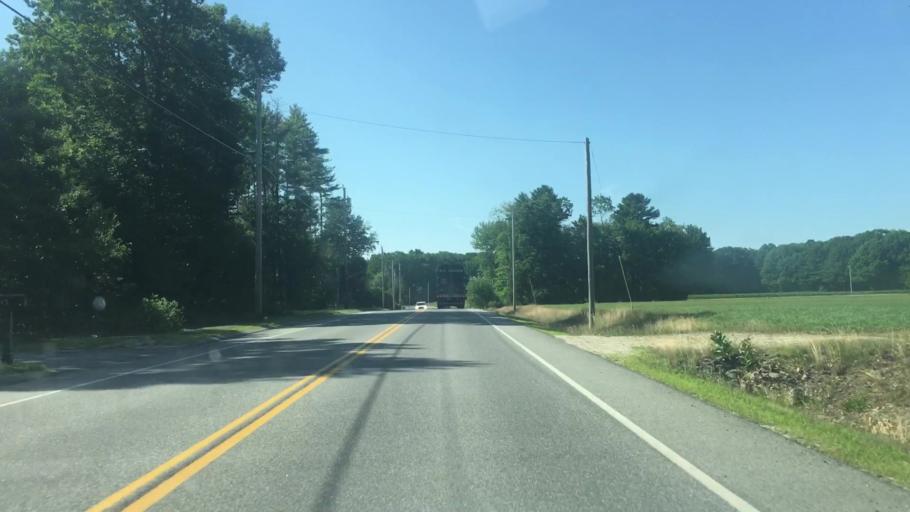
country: US
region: Maine
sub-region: York County
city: Buxton
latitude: 43.5924
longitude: -70.5262
